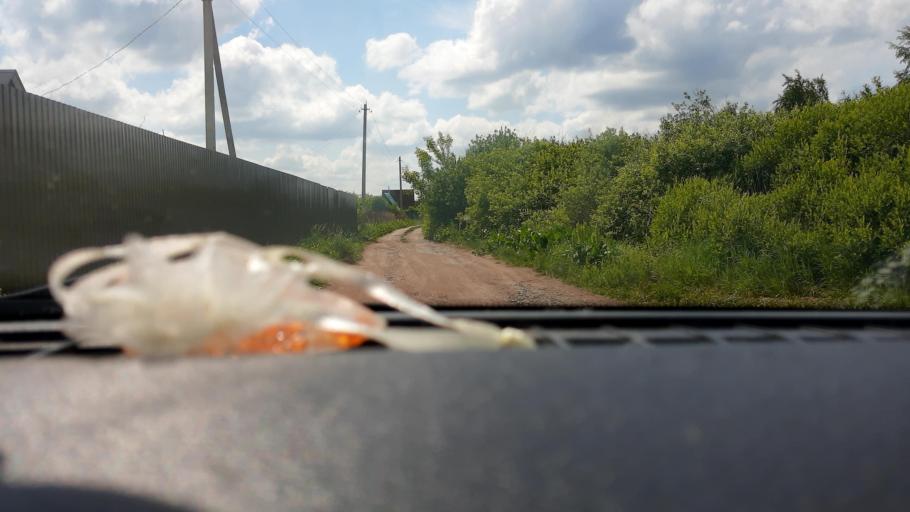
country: RU
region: Bashkortostan
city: Asanovo
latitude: 54.9187
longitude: 55.6313
